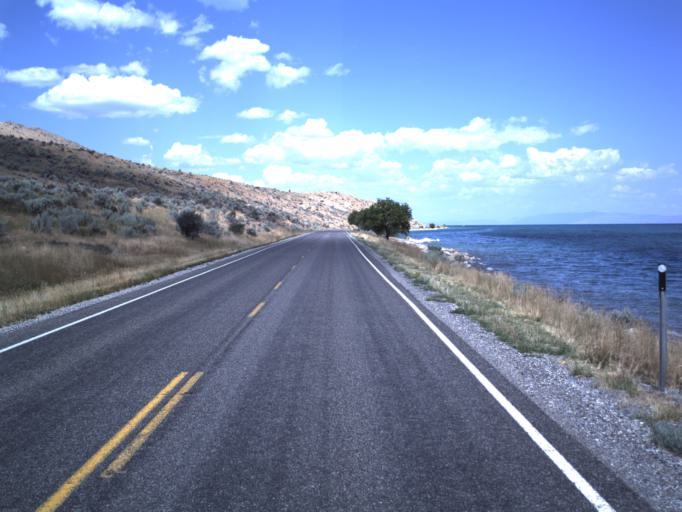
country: US
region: Utah
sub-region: Rich County
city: Randolph
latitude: 41.8674
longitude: -111.3649
